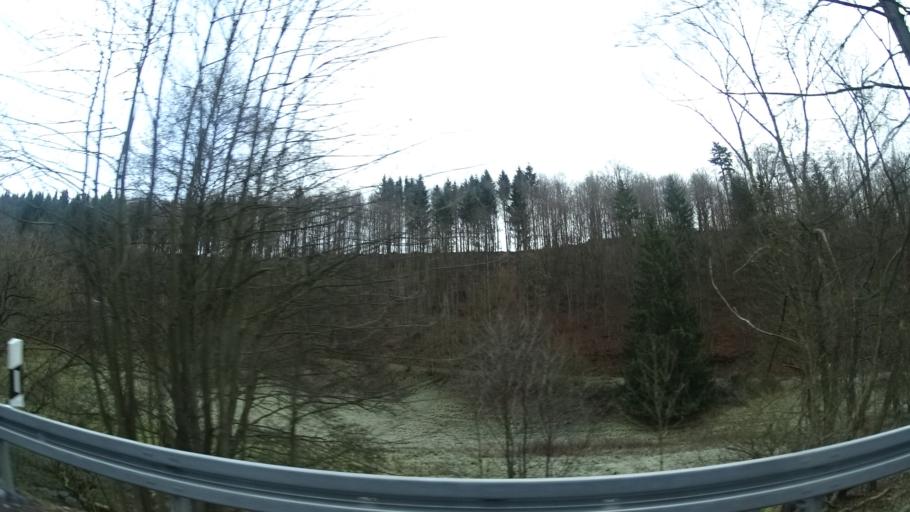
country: DE
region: Thuringia
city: Pappenheim
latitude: 50.8049
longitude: 10.4715
